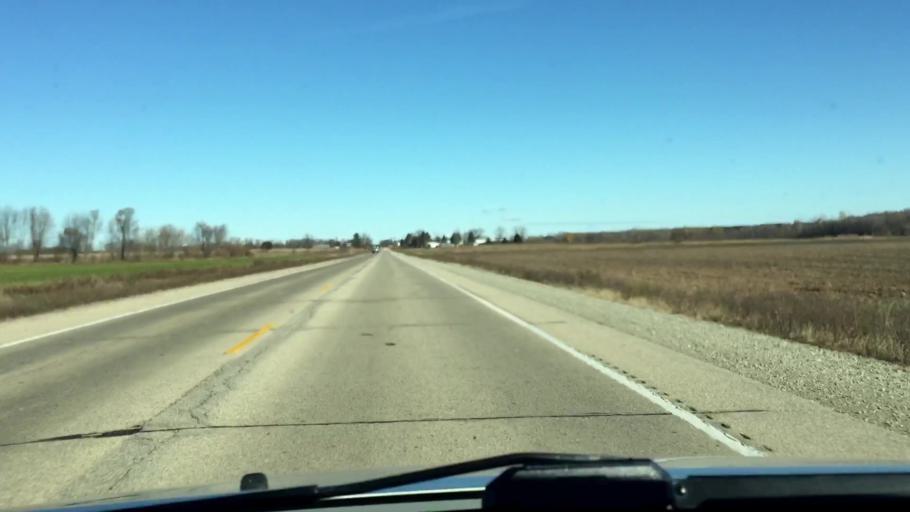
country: US
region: Wisconsin
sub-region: Brown County
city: Pulaski
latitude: 44.6322
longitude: -88.2202
